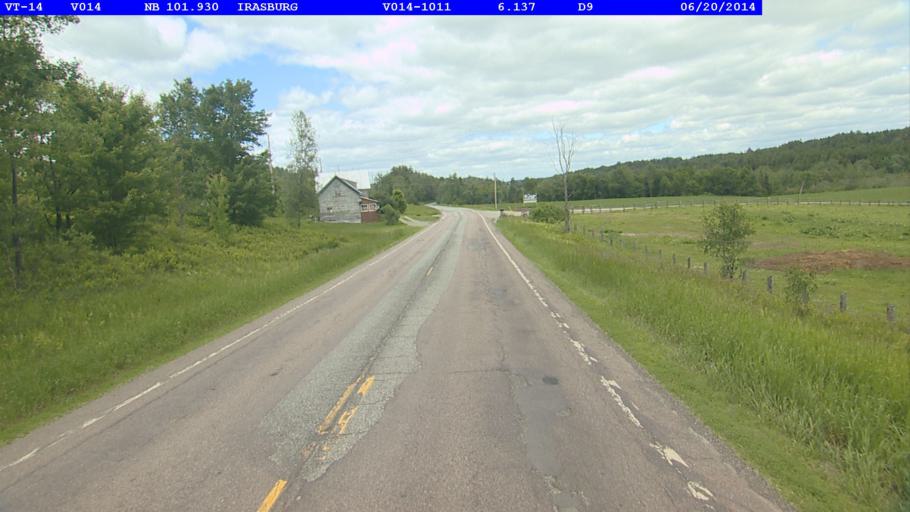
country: US
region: Vermont
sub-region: Orleans County
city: Newport
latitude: 44.8454
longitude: -72.2817
